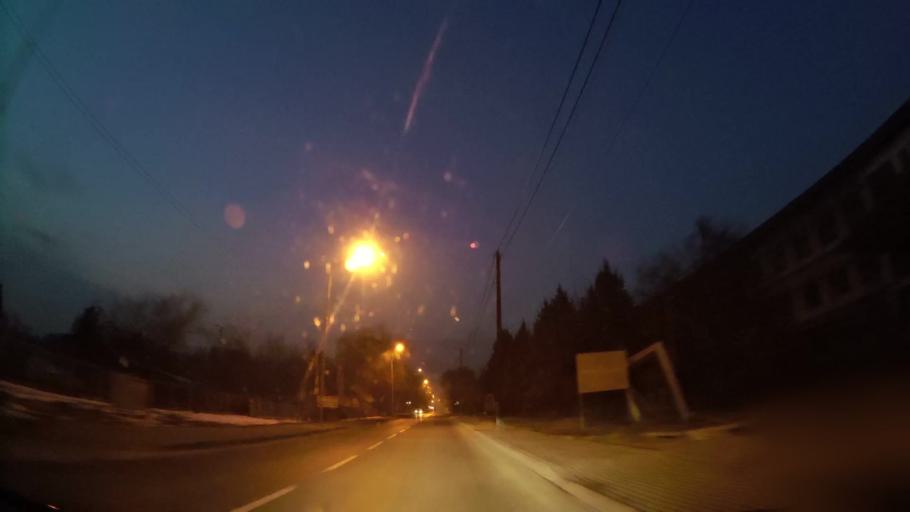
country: MK
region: Cair
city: Cair
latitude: 42.0022
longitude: 21.4818
